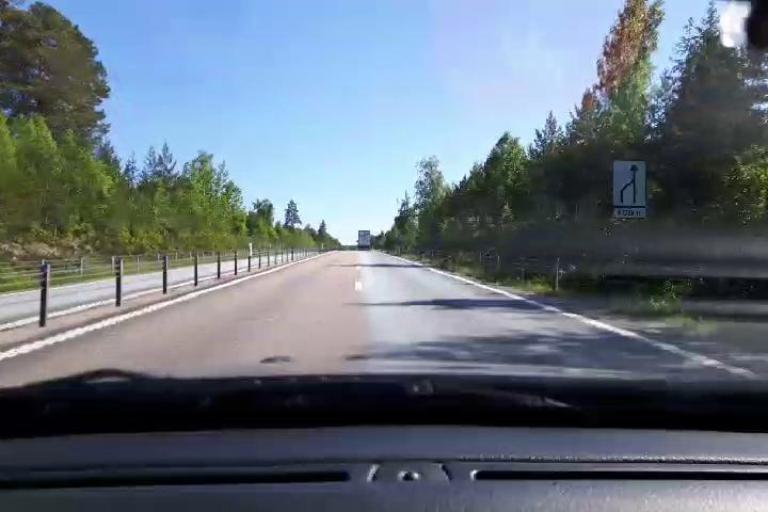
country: SE
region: Gaevleborg
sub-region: Soderhamns Kommun
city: Soderhamn
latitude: 61.2684
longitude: 17.0280
